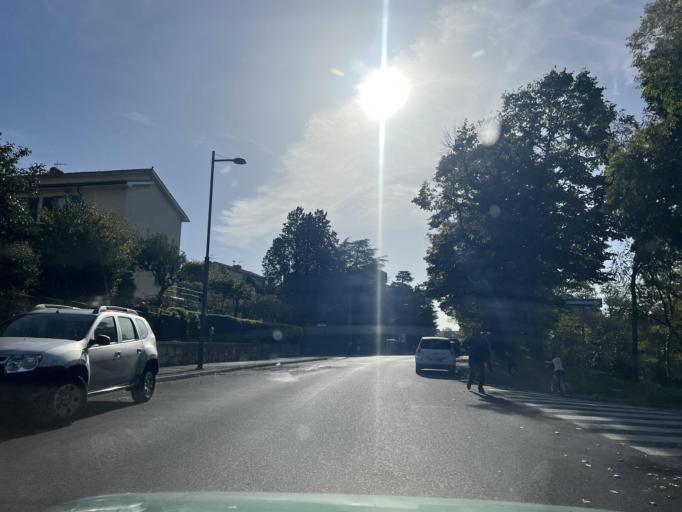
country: IT
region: Friuli Venezia Giulia
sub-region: Provincia di Trieste
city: Domio
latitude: 45.6191
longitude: 13.8256
